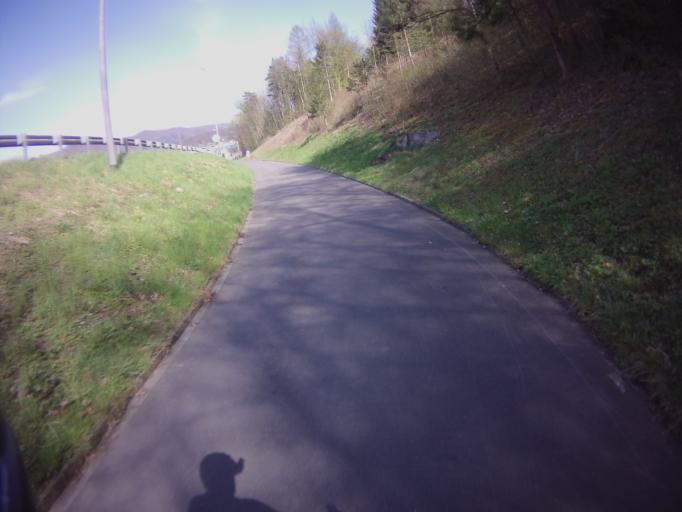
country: CH
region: Aargau
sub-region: Bezirk Baden
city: Neuenhof
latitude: 47.4528
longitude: 8.3147
